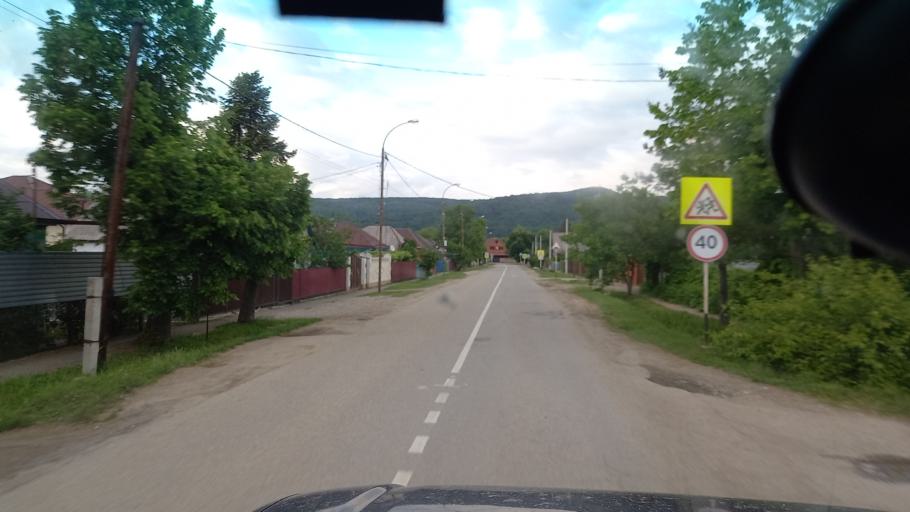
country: RU
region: Krasnodarskiy
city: Apsheronsk
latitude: 44.4556
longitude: 39.7473
